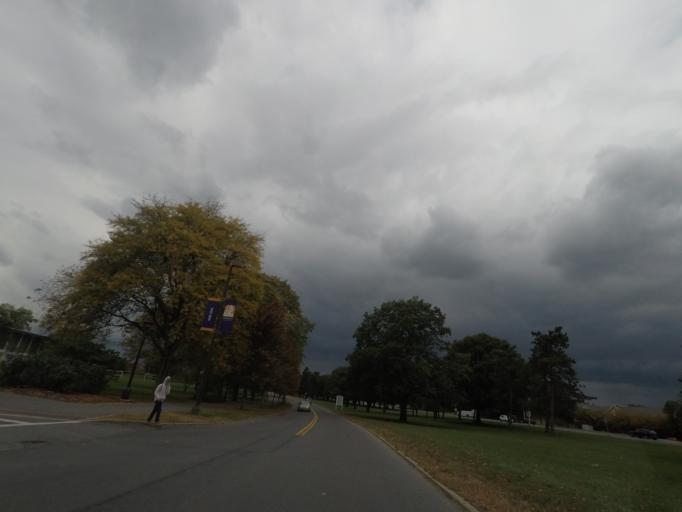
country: US
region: New York
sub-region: Albany County
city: Roessleville
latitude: 42.6872
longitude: -73.8172
